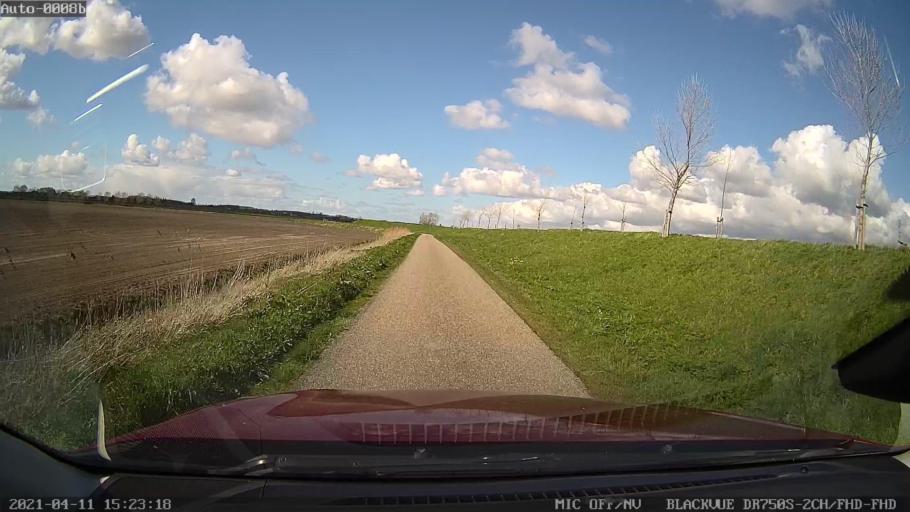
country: NL
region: Zeeland
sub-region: Schouwen-Duiveland
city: Bruinisse
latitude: 51.6560
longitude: 4.0244
